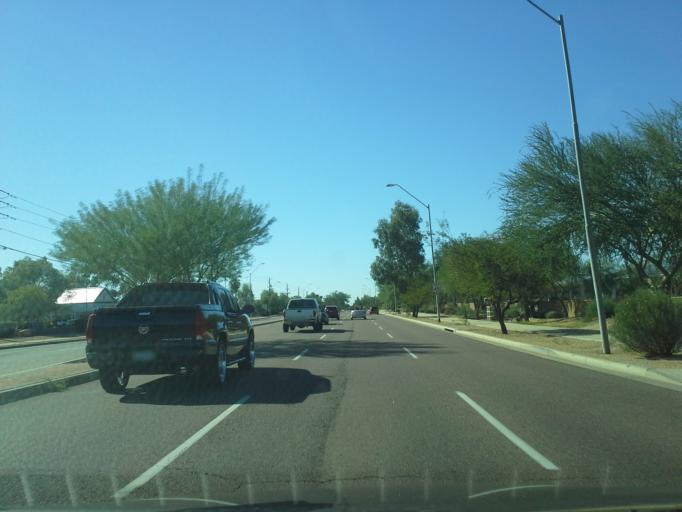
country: US
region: Arizona
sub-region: Maricopa County
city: Paradise Valley
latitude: 33.6405
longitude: -111.9437
